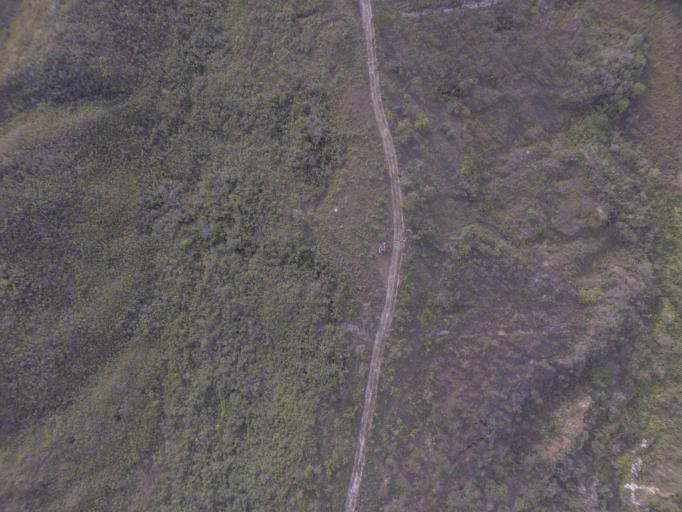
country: BR
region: Minas Gerais
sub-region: Tiradentes
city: Tiradentes
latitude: -21.0573
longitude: -44.1040
